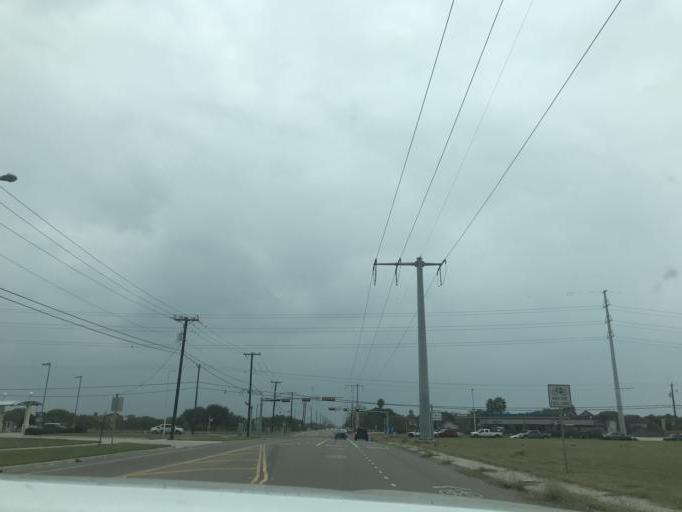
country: US
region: Texas
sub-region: Nueces County
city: Corpus Christi
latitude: 27.6772
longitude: -97.3502
